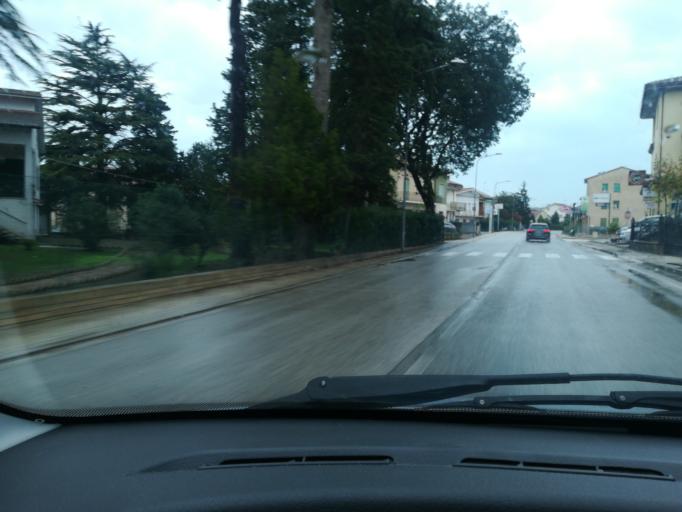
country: IT
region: The Marches
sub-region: Provincia di Macerata
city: Borgo Stazione
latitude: 43.2846
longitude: 13.6430
